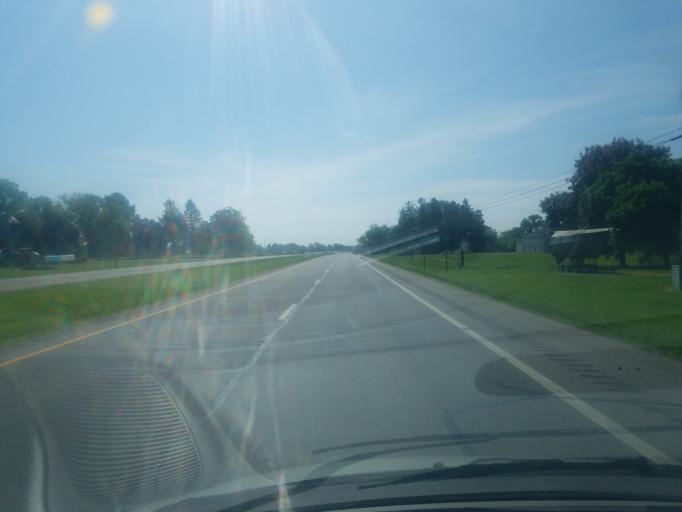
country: US
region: Ohio
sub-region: Huron County
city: Monroeville
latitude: 41.2605
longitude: -82.7664
